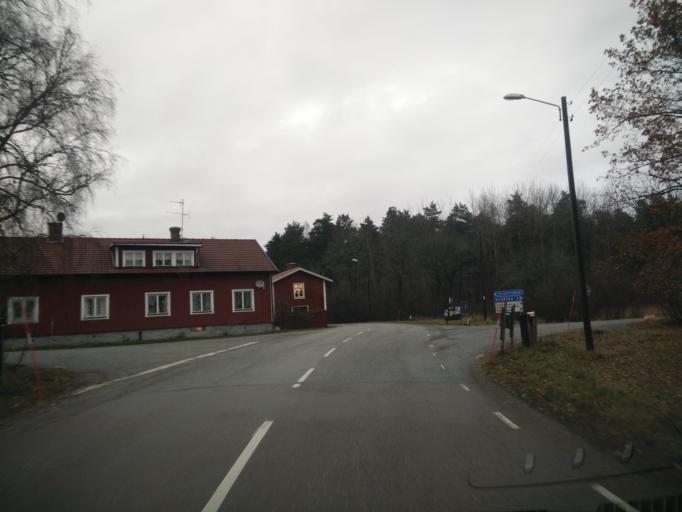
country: SE
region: Uppsala
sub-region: Enkopings Kommun
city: Enkoping
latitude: 59.8129
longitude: 17.1002
